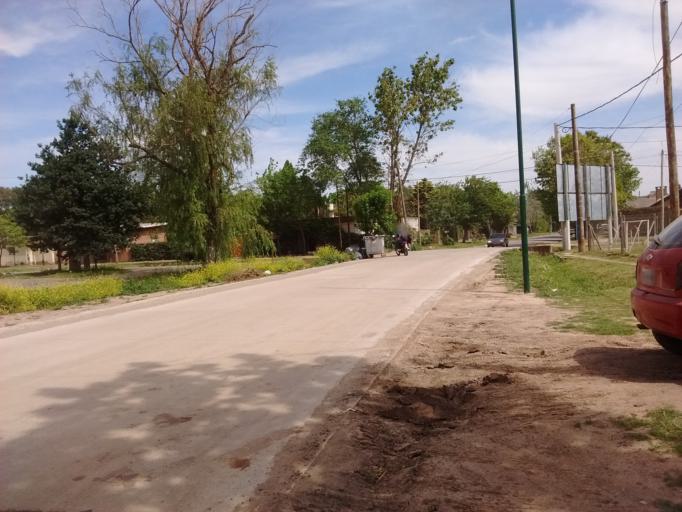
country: AR
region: Santa Fe
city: Funes
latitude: -32.9103
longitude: -60.8044
